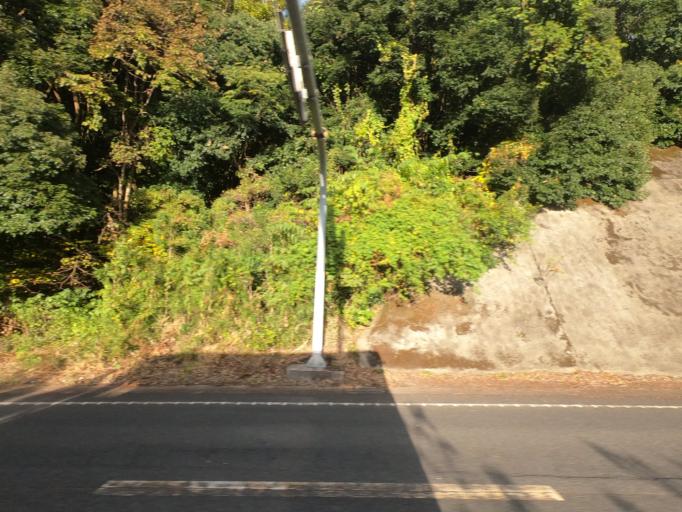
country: JP
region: Kumamoto
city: Minamata
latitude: 32.2440
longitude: 130.4790
